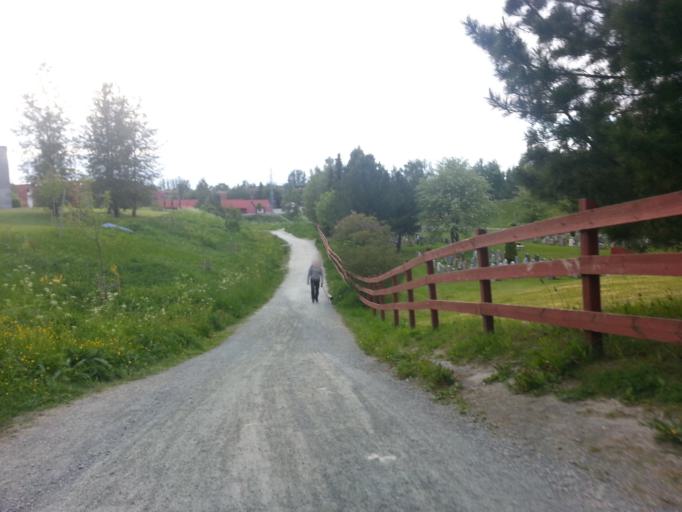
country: NO
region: Sor-Trondelag
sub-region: Trondheim
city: Trondheim
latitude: 63.4129
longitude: 10.4399
